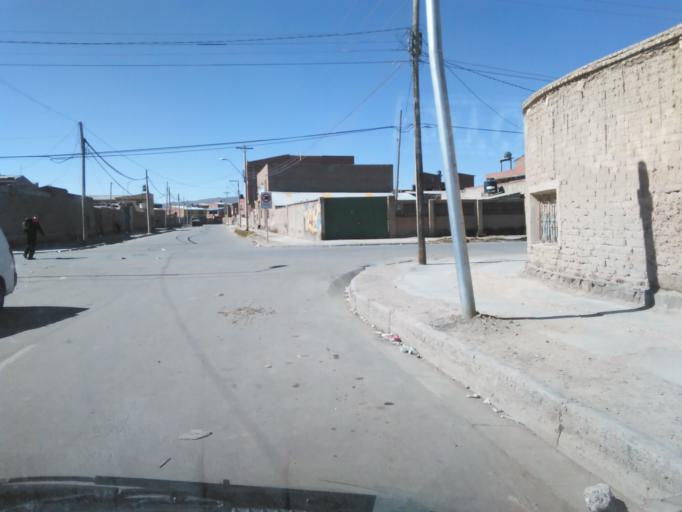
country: BO
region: Oruro
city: Oruro
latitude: -17.9682
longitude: -67.0966
